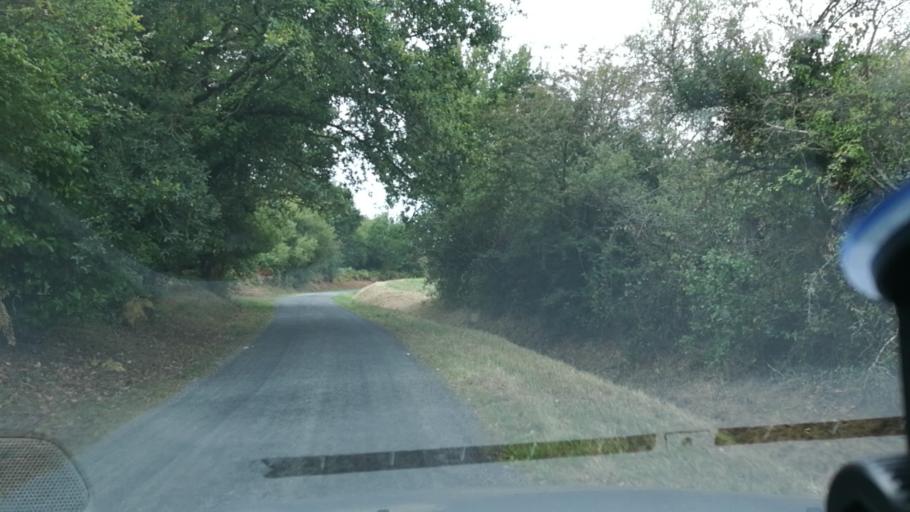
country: FR
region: Brittany
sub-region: Departement d'Ille-et-Vilaine
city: Saint-Jacques-de-la-Lande
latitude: 48.0910
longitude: -1.7311
